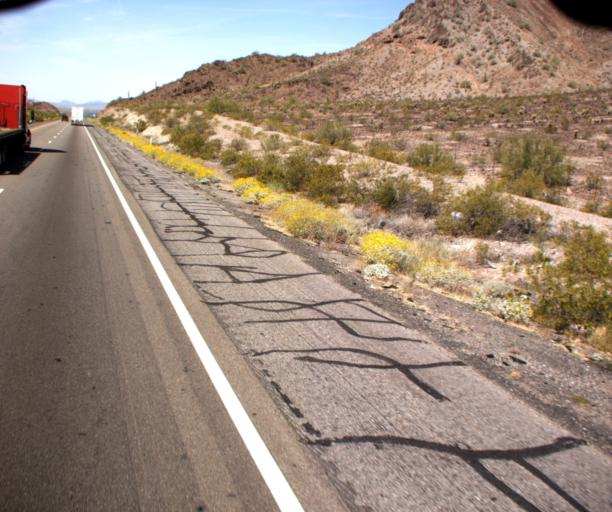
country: US
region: Arizona
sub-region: La Paz County
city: Salome
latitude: 33.6114
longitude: -113.6335
